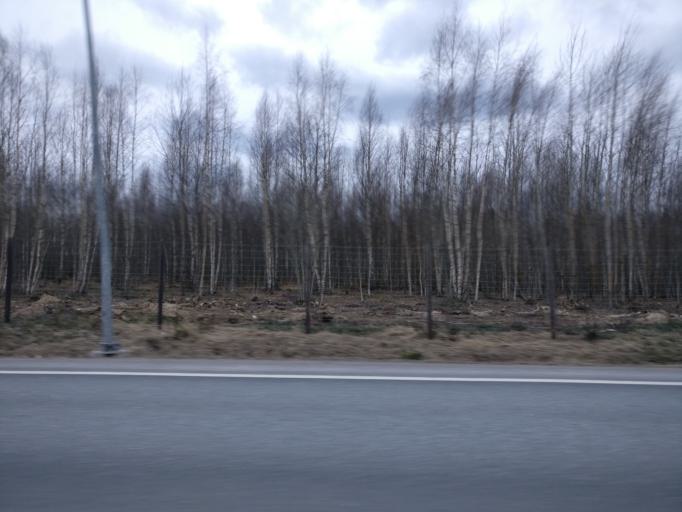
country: FI
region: Haeme
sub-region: Riihimaeki
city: Riihimaeki
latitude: 60.7196
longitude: 24.7306
